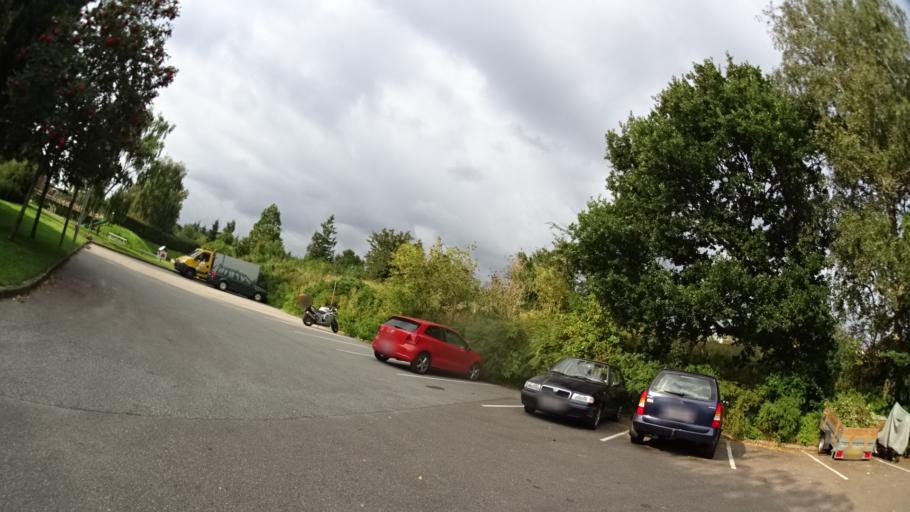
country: DK
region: Central Jutland
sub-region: Arhus Kommune
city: Stavtrup
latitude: 56.1513
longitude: 10.1215
